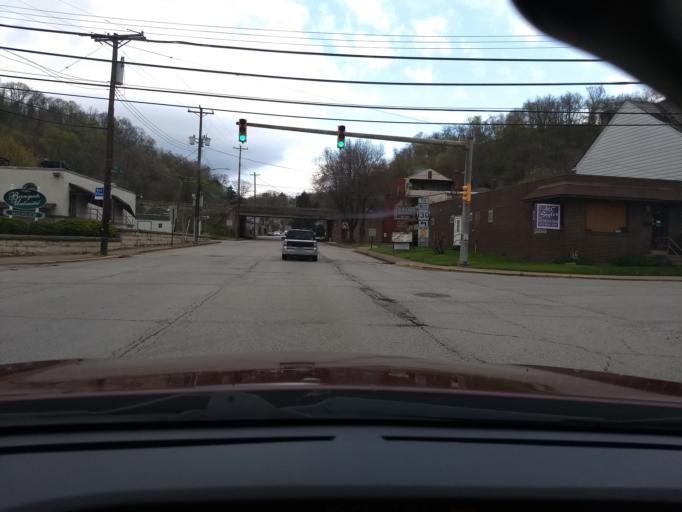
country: US
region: Pennsylvania
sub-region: Allegheny County
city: Wilmerding
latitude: 40.3954
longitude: -79.8047
